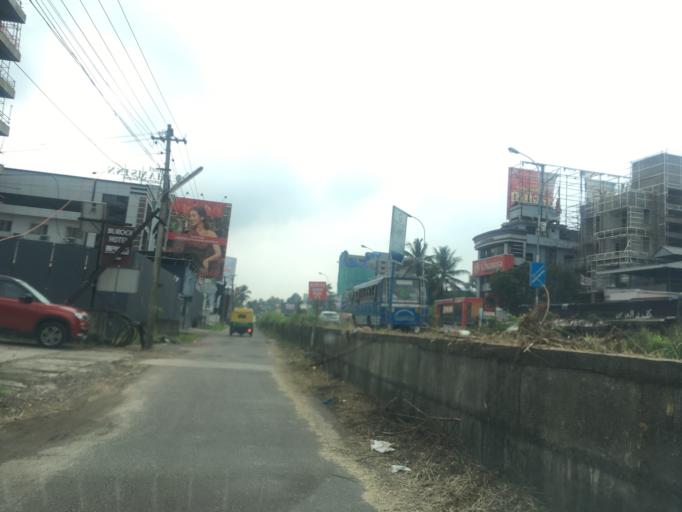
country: IN
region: Kerala
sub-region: Ernakulam
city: Elur
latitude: 10.0307
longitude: 76.3051
